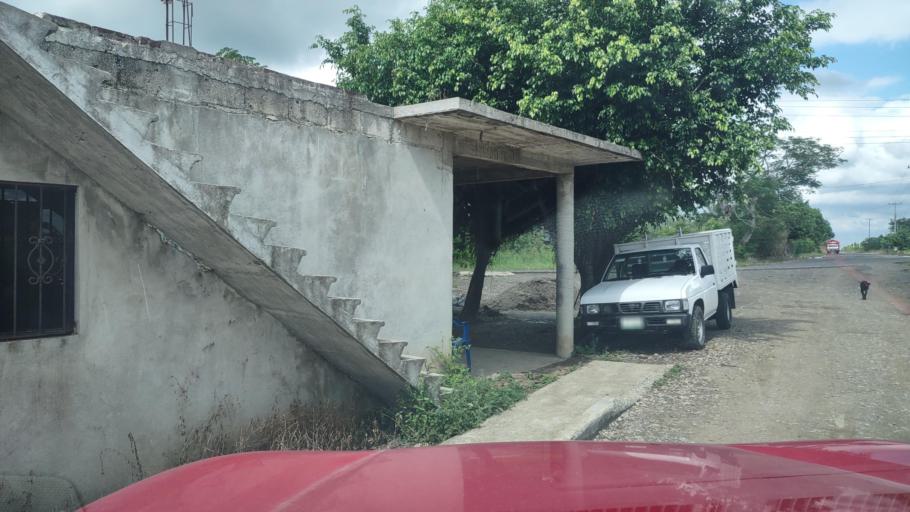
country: MX
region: Veracruz
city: Gutierrez Zamora
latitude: 20.2853
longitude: -97.1292
